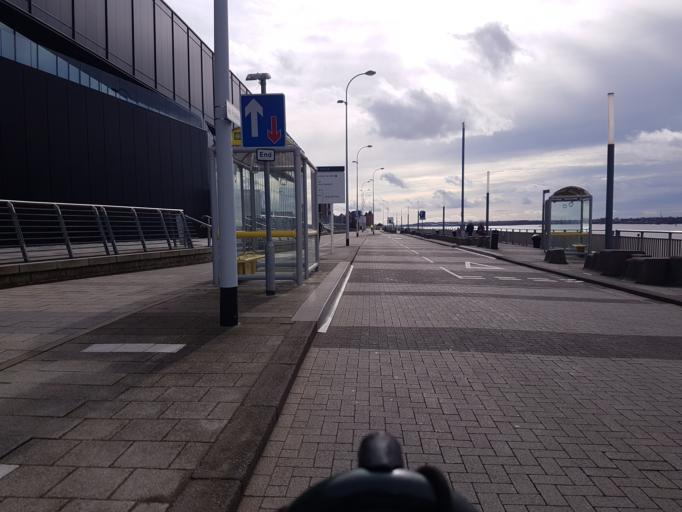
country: GB
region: England
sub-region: Liverpool
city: Liverpool
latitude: 53.3954
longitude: -2.9910
